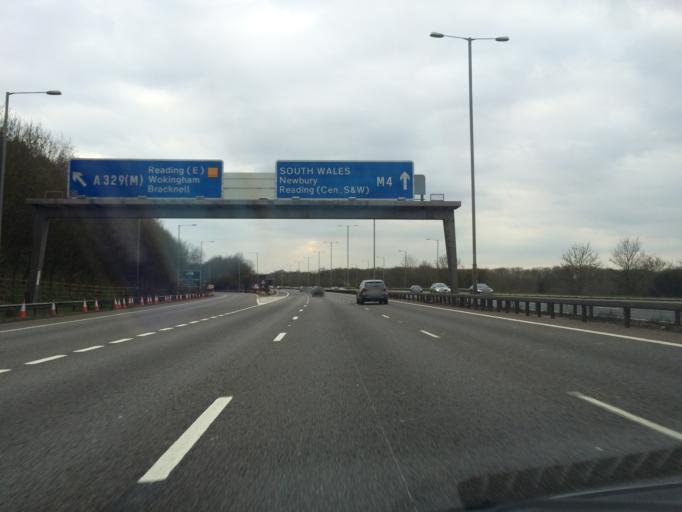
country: GB
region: England
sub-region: Wokingham
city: Wokingham
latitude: 51.4360
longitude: -0.8442
